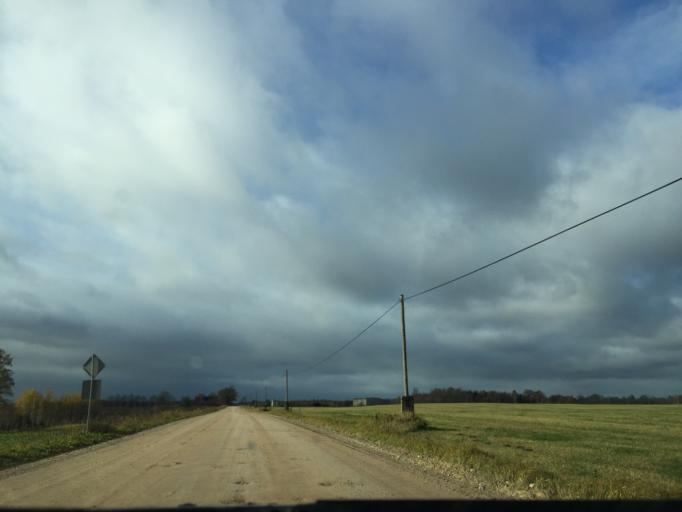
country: LV
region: Tukuma Rajons
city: Tukums
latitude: 56.9724
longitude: 23.0881
